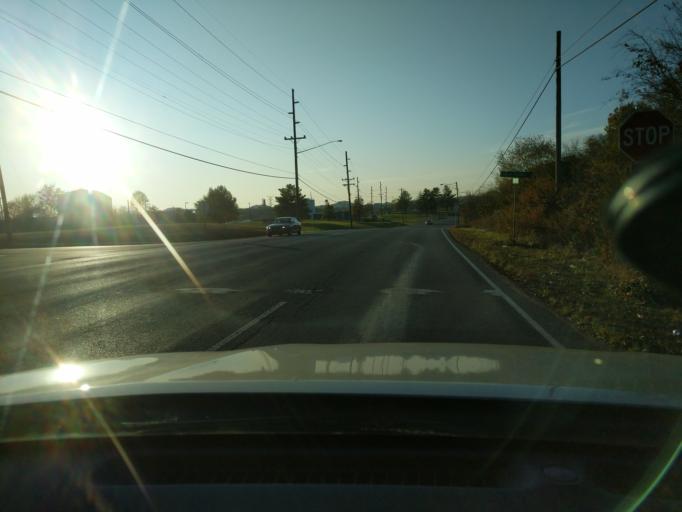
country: US
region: Tennessee
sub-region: Davidson County
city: Nashville
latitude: 36.1827
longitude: -86.8474
